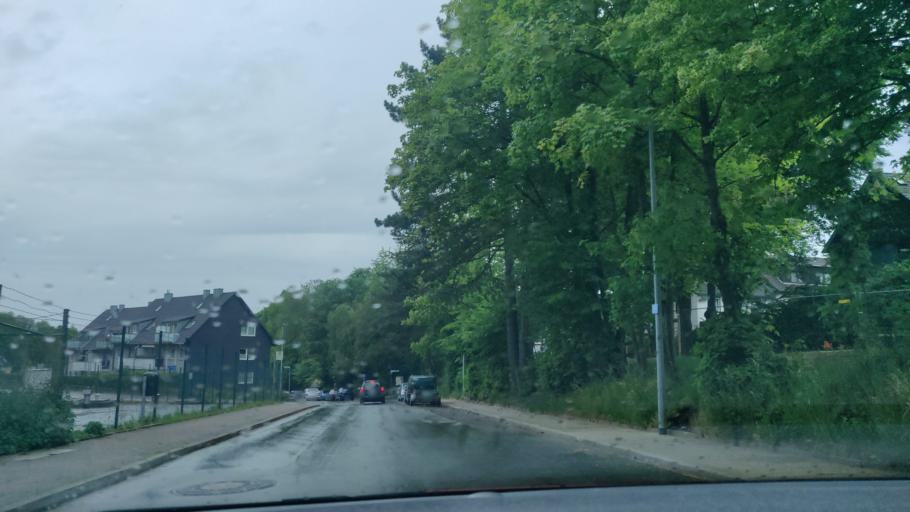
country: DE
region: North Rhine-Westphalia
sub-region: Regierungsbezirk Dusseldorf
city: Heiligenhaus
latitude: 51.3324
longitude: 6.9536
